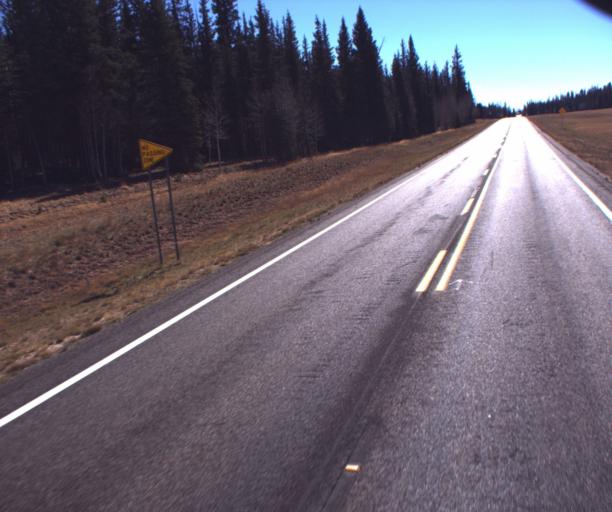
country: US
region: Arizona
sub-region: Coconino County
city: Grand Canyon
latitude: 36.3454
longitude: -112.1174
